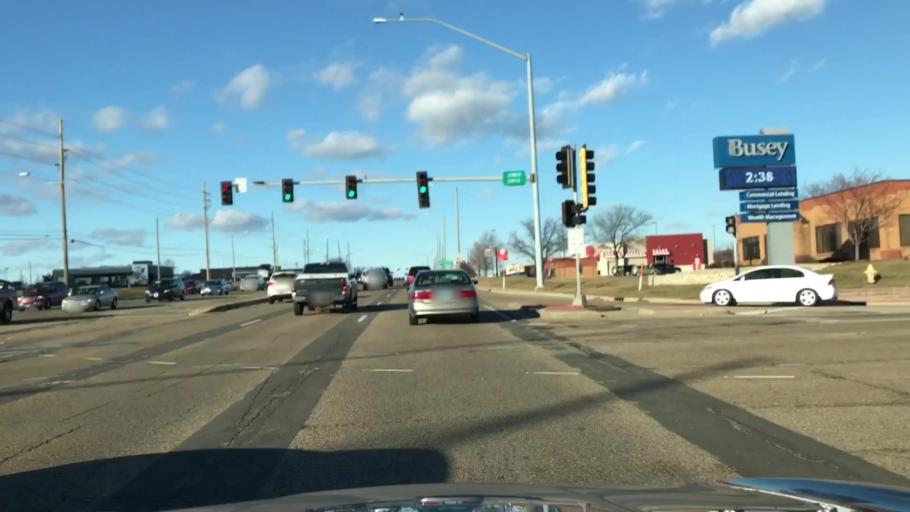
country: US
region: Illinois
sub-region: McLean County
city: Normal
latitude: 40.5063
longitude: -88.9531
